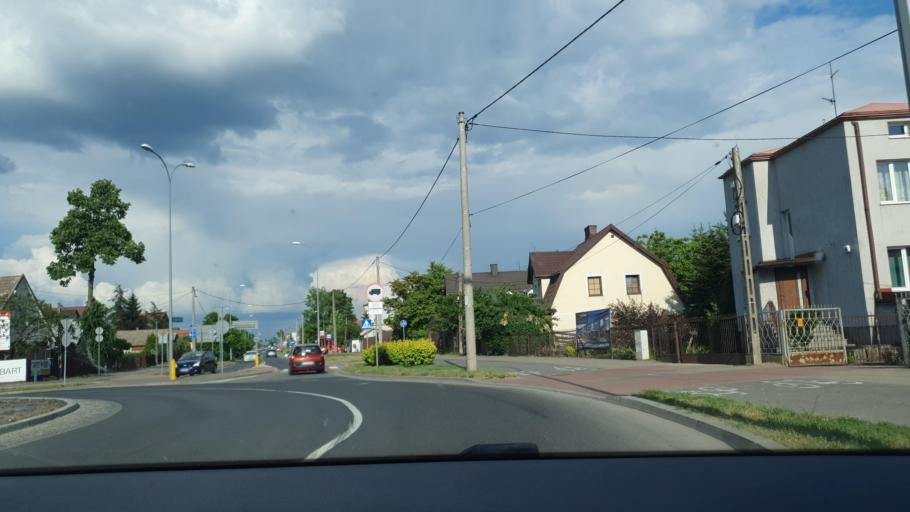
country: PL
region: Podlasie
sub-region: Bialystok
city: Bialystok
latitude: 53.1219
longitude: 23.2028
